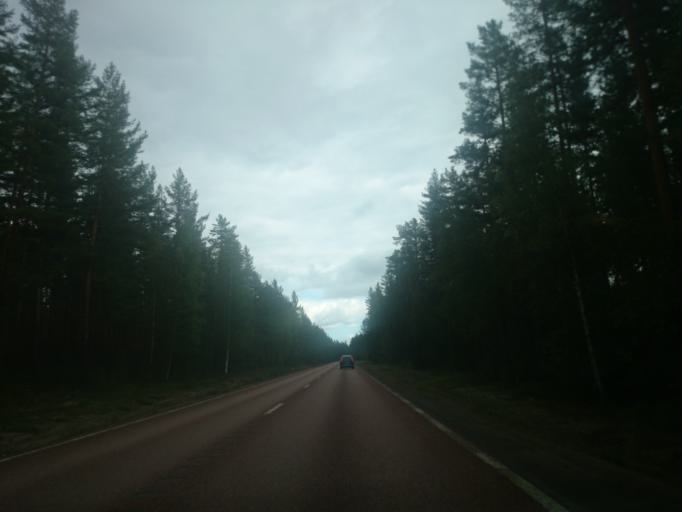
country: SE
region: Gaevleborg
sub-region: Ljusdals Kommun
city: Farila
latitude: 61.9246
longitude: 15.5873
